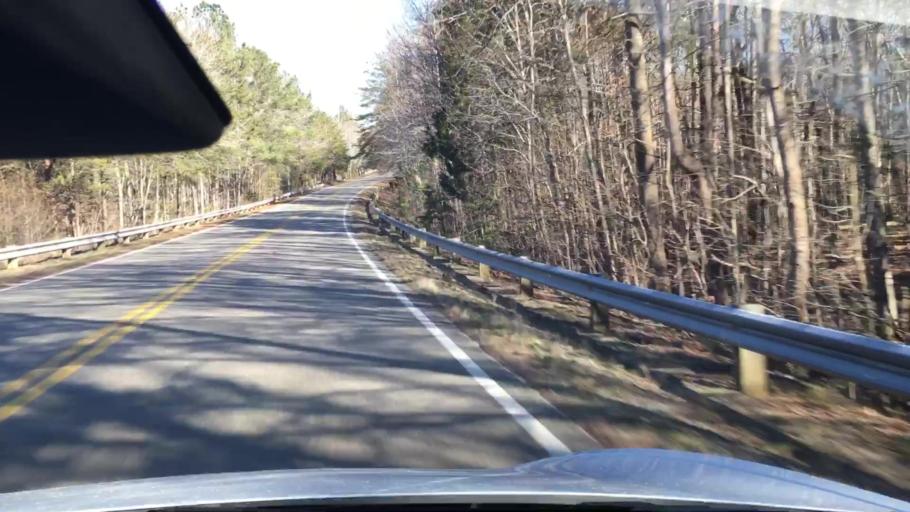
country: US
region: Virginia
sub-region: Powhatan County
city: Powhatan
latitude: 37.5316
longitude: -77.8007
